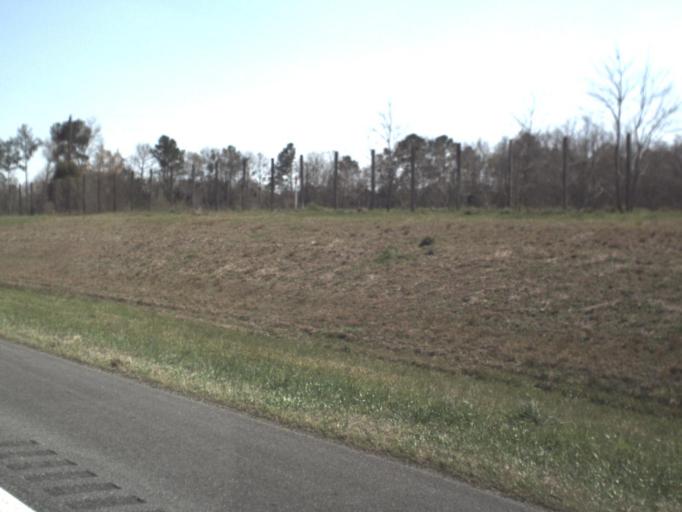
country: US
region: Florida
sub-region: Jackson County
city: Marianna
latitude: 30.7384
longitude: -85.2416
